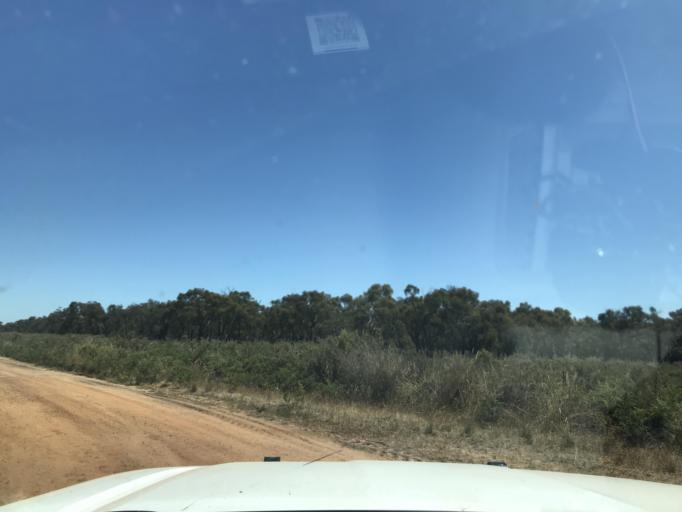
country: AU
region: South Australia
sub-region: Wattle Range
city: Penola
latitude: -37.0432
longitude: 141.4331
